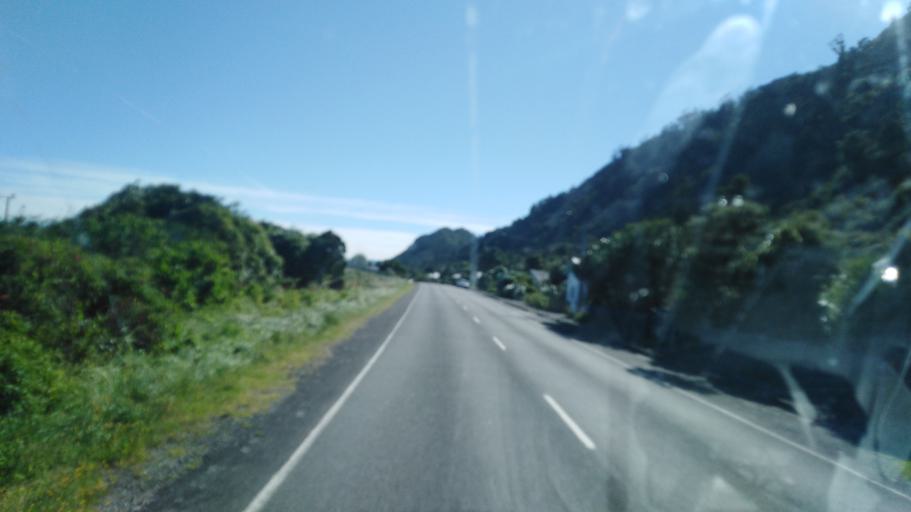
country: NZ
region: West Coast
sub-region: Buller District
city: Westport
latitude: -41.6382
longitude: 171.8465
